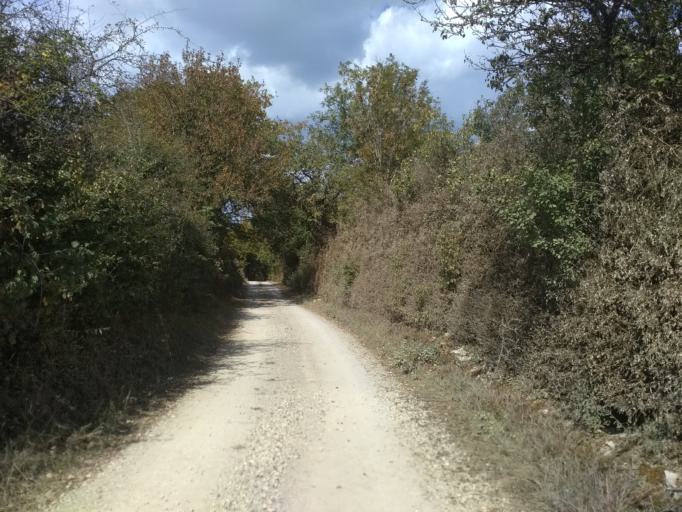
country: FR
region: Midi-Pyrenees
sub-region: Departement de l'Aveyron
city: Bozouls
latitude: 44.4637
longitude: 2.6743
